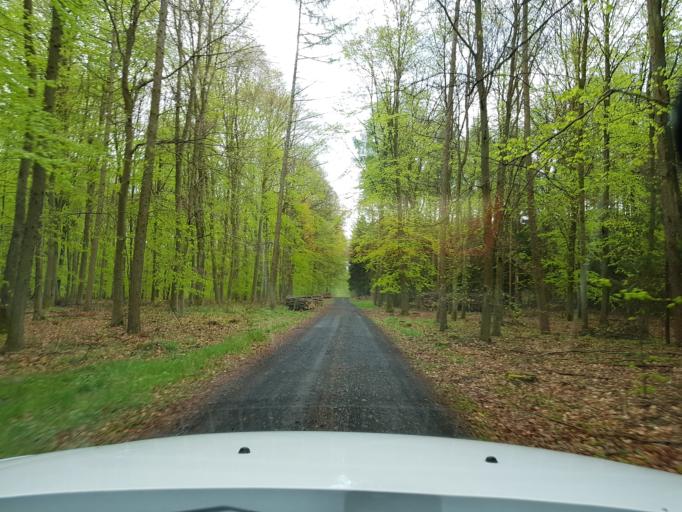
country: PL
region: West Pomeranian Voivodeship
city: Trzcinsko Zdroj
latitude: 52.9961
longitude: 14.6474
